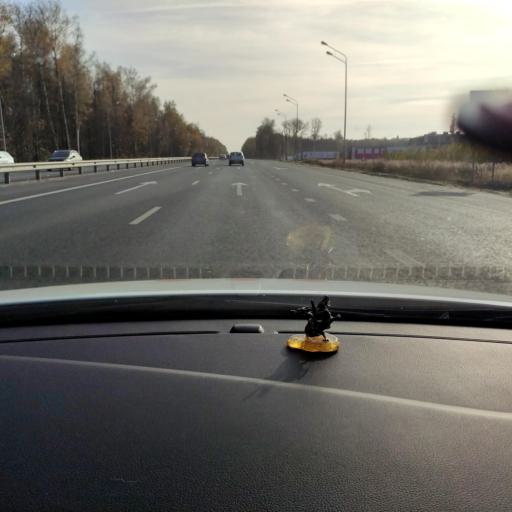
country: RU
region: Tatarstan
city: Osinovo
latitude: 55.8500
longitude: 48.8530
